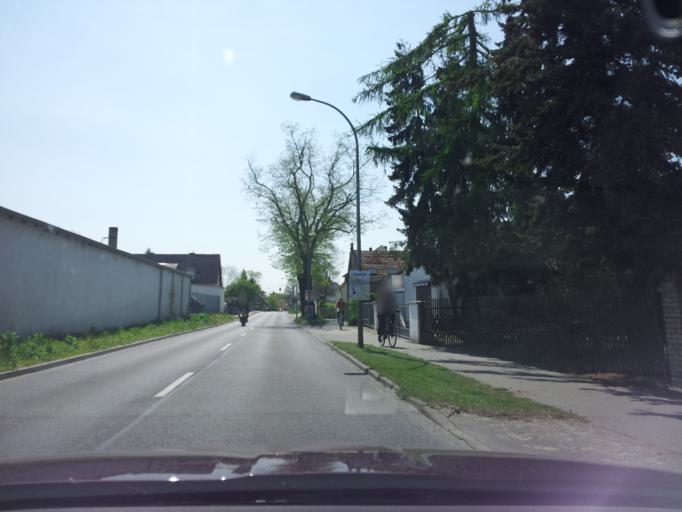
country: DE
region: Brandenburg
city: Stahnsdorf
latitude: 52.3696
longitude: 13.1983
